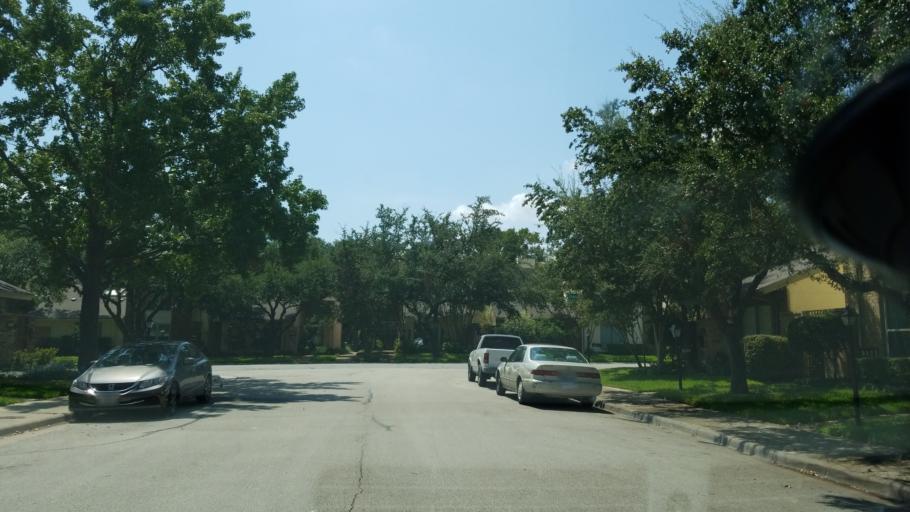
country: US
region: Texas
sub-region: Dallas County
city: Richardson
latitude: 32.9212
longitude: -96.7361
